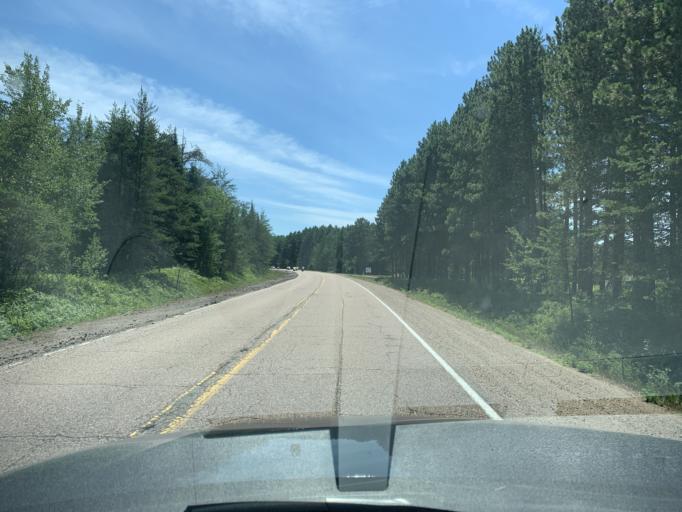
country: CA
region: Ontario
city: Petawawa
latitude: 45.6553
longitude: -77.5803
